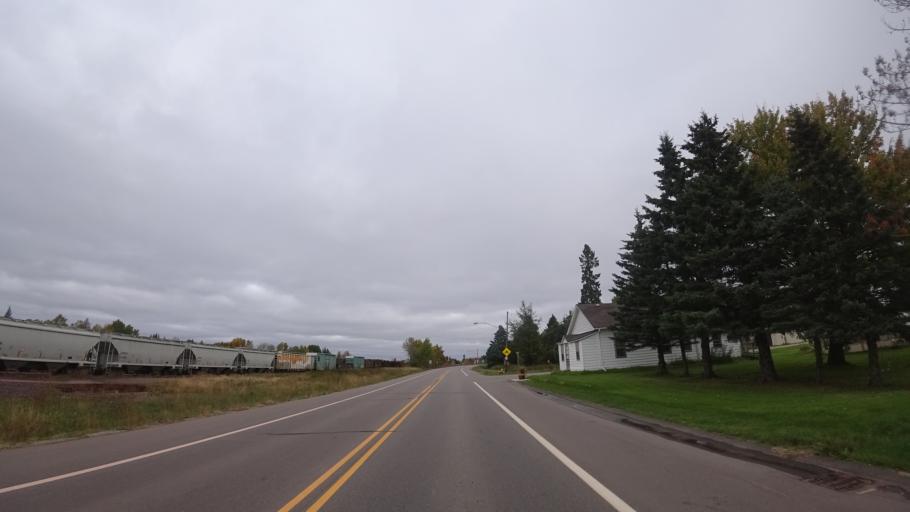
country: US
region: Michigan
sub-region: Iron County
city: Crystal Falls
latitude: 46.1422
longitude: -88.0940
